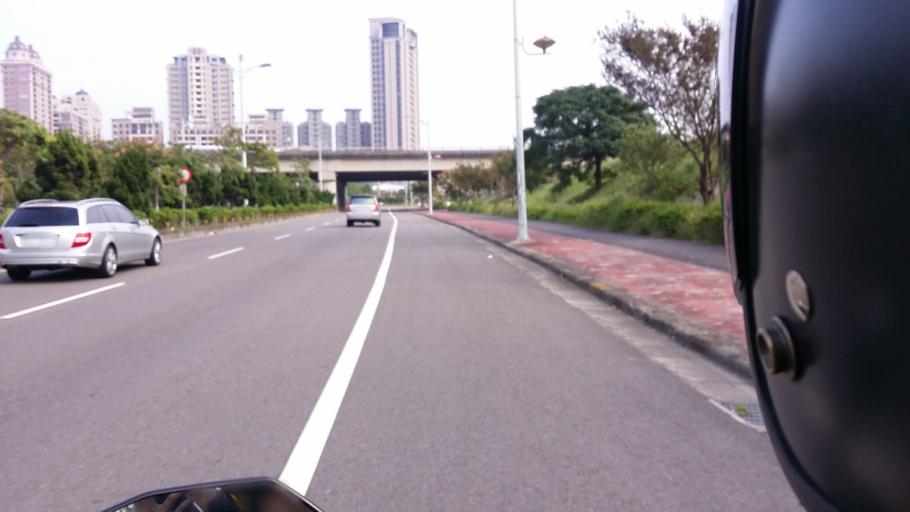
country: TW
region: Taiwan
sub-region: Hsinchu
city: Zhubei
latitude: 24.8174
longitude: 121.0119
